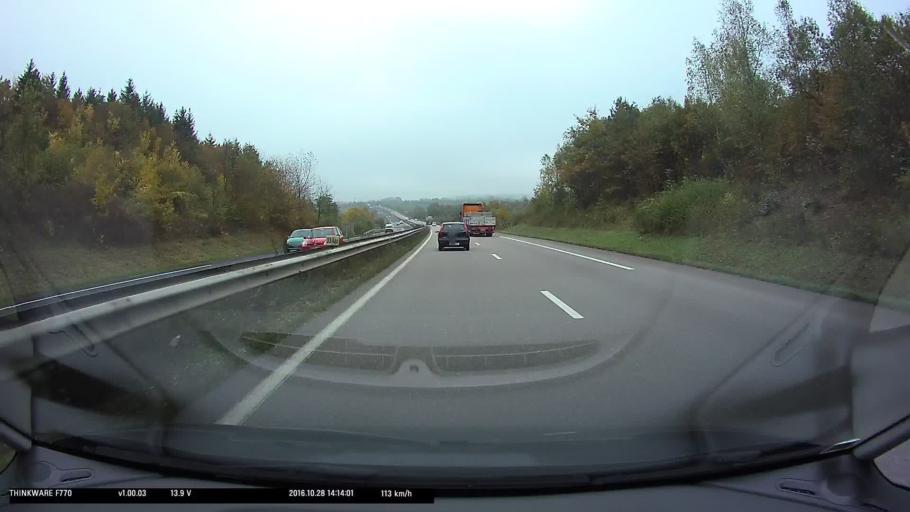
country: FR
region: Lorraine
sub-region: Departement de Meurthe-et-Moselle
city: Luneville
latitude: 48.5792
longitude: 6.4648
